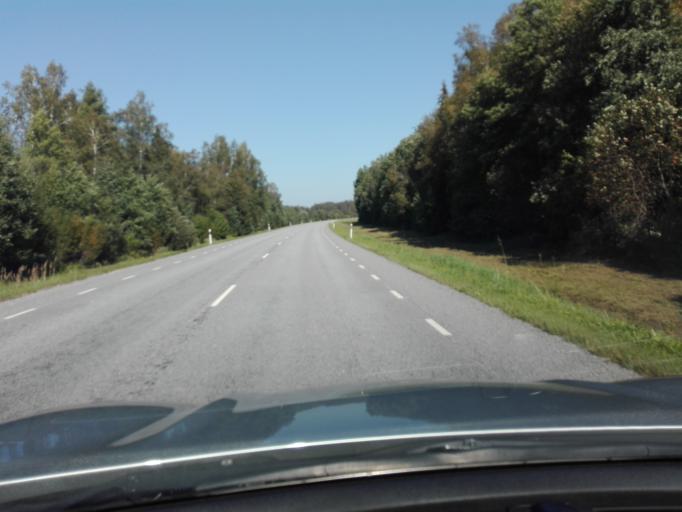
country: EE
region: Raplamaa
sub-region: Rapla vald
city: Rapla
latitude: 59.0117
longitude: 24.7725
